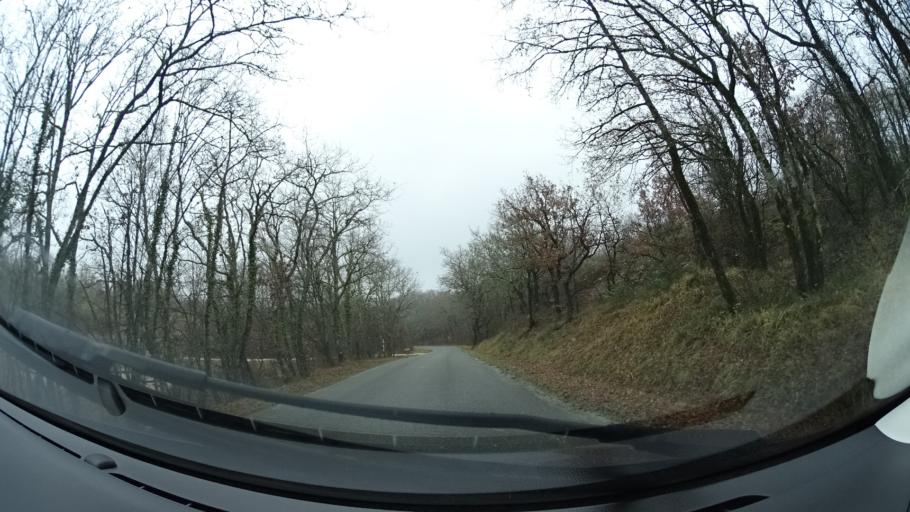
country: FR
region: Midi-Pyrenees
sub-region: Departement du Lot
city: Montcuq
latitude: 44.3848
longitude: 1.2244
